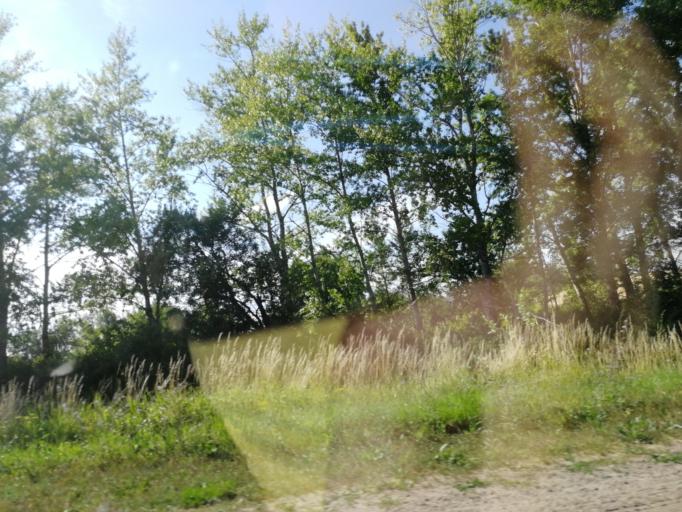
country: RU
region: Tula
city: Tovarkovskiy
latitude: 53.6342
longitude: 38.2467
